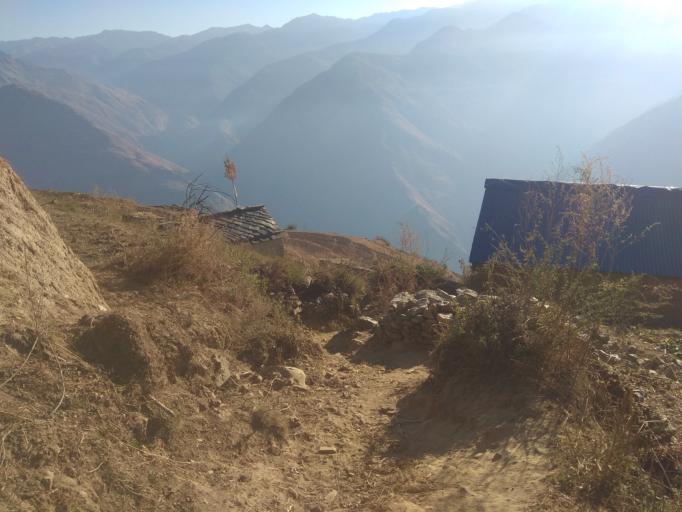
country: NP
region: Mid Western
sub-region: Karnali Zone
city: Jumla
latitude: 29.3140
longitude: 81.7318
